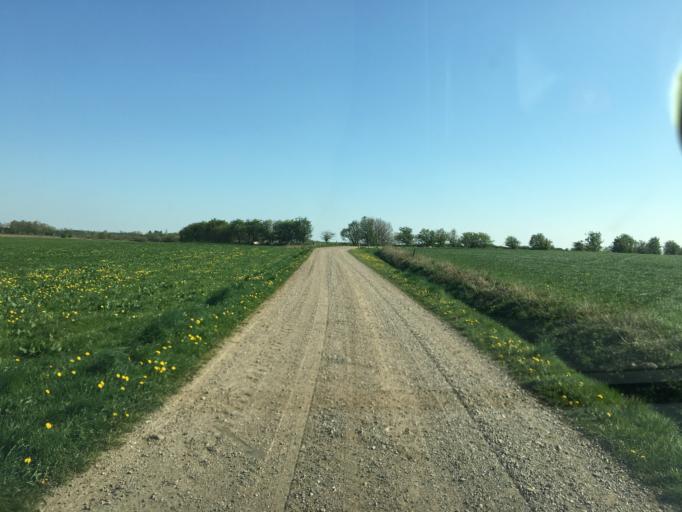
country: DK
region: South Denmark
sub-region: Tonder Kommune
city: Toftlund
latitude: 55.1658
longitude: 9.0973
